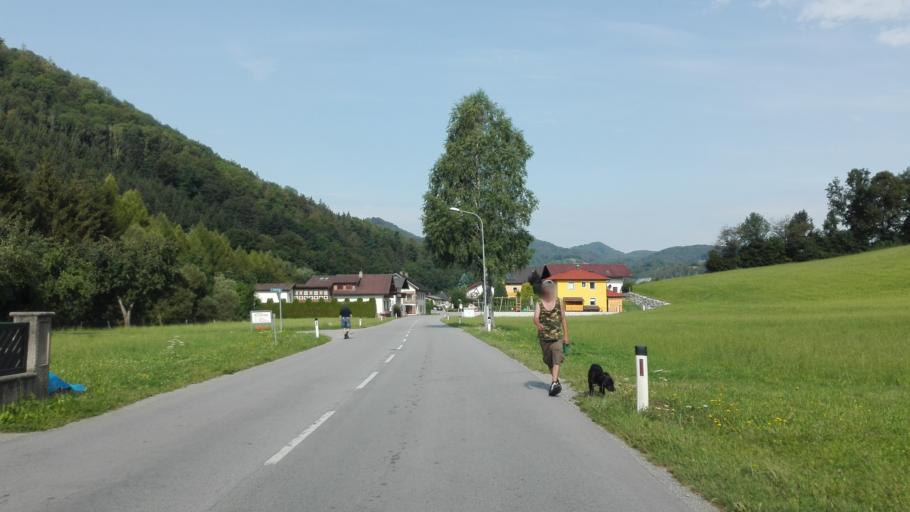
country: AT
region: Lower Austria
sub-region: Politischer Bezirk Sankt Polten
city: Rabenstein an der Pielach
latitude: 48.0327
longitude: 15.4638
